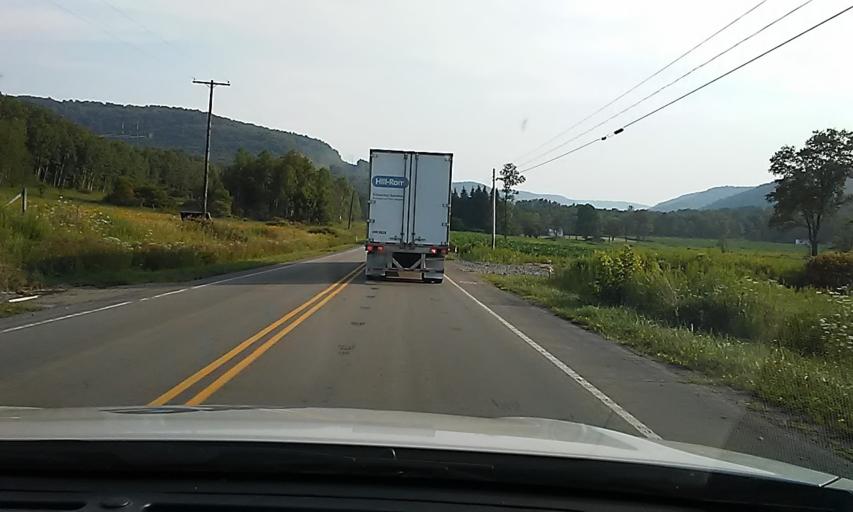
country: US
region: Pennsylvania
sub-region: McKean County
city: Smethport
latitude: 41.7542
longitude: -78.5243
